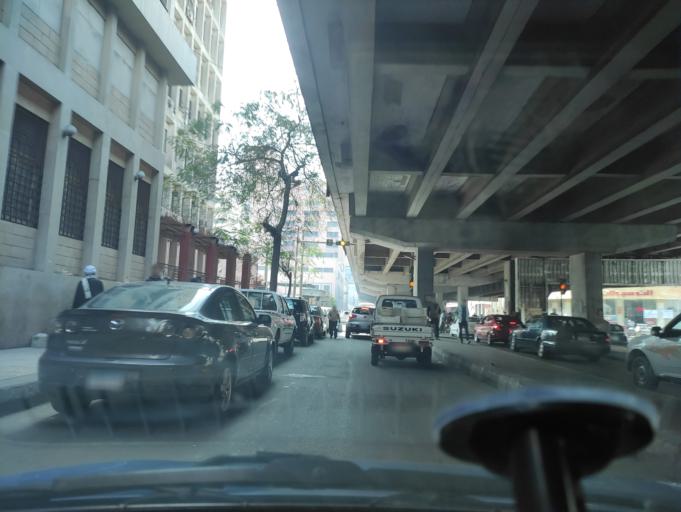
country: EG
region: Muhafazat al Qahirah
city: Cairo
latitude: 30.0600
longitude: 31.2448
